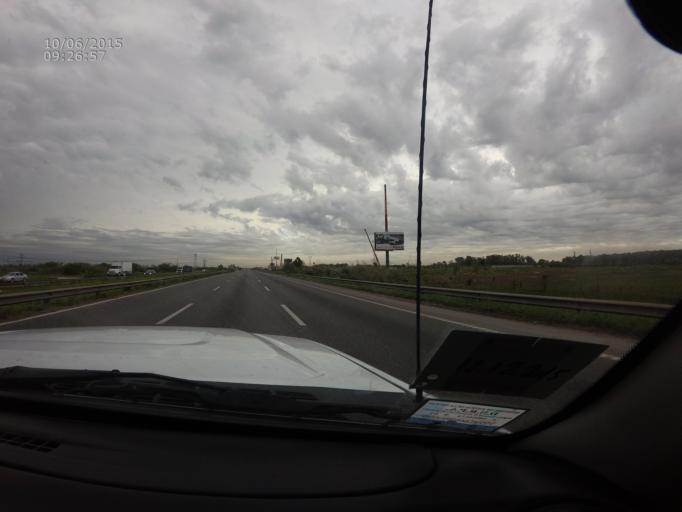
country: AR
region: Buenos Aires
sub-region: Partido de Campana
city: Campana
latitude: -34.1721
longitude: -58.9860
